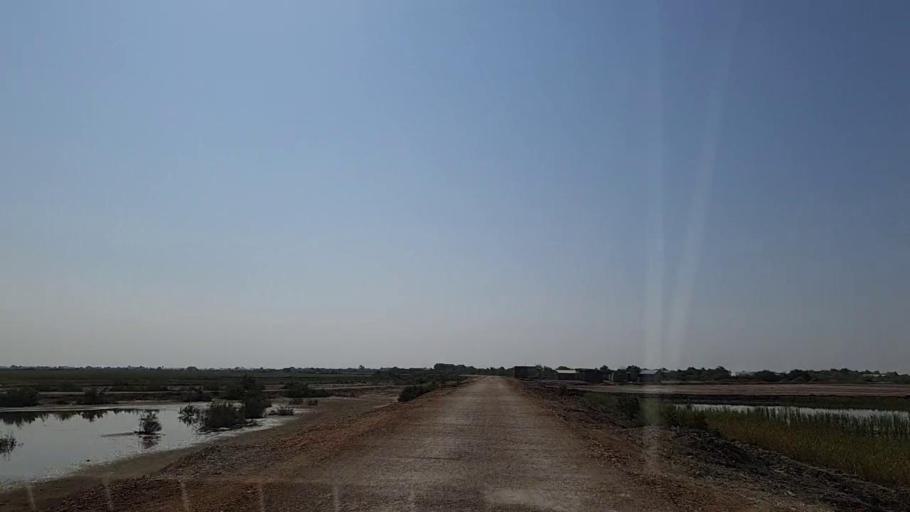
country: PK
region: Sindh
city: Chuhar Jamali
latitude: 24.4757
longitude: 68.0912
